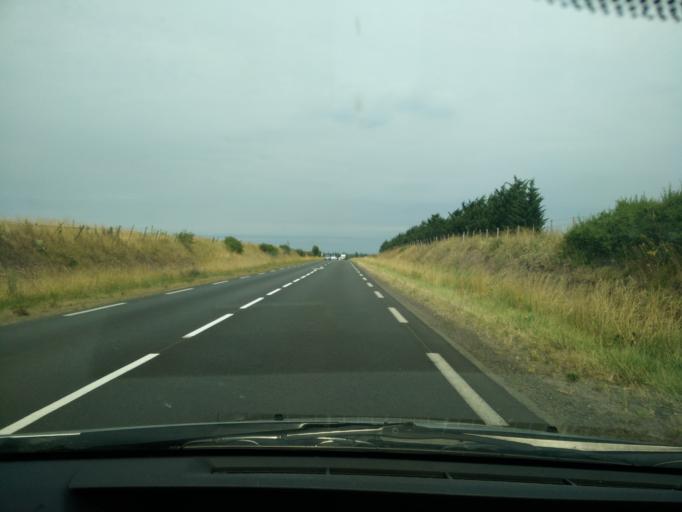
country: FR
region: Pays de la Loire
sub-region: Departement de Maine-et-Loire
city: Doue-la-Fontaine
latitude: 47.1825
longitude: -0.2876
